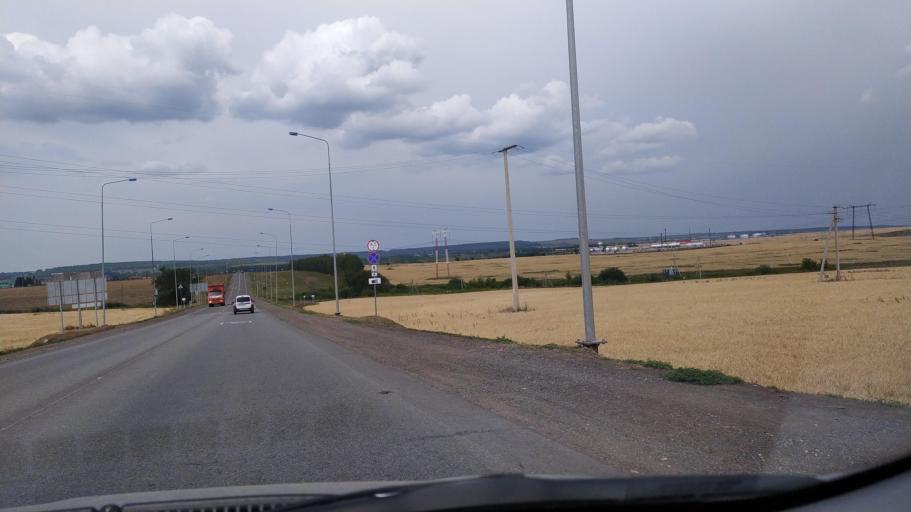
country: RU
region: Tatarstan
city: Al'met'yevsk
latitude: 54.9017
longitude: 52.2240
